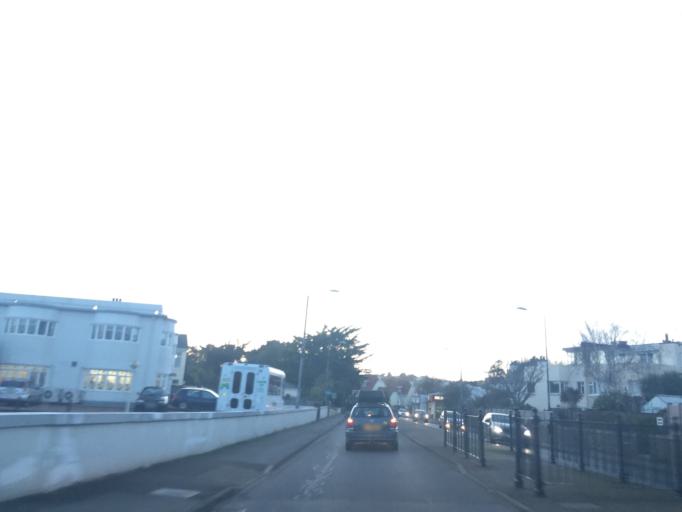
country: JE
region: St Helier
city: Saint Helier
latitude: 49.1971
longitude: -2.1455
